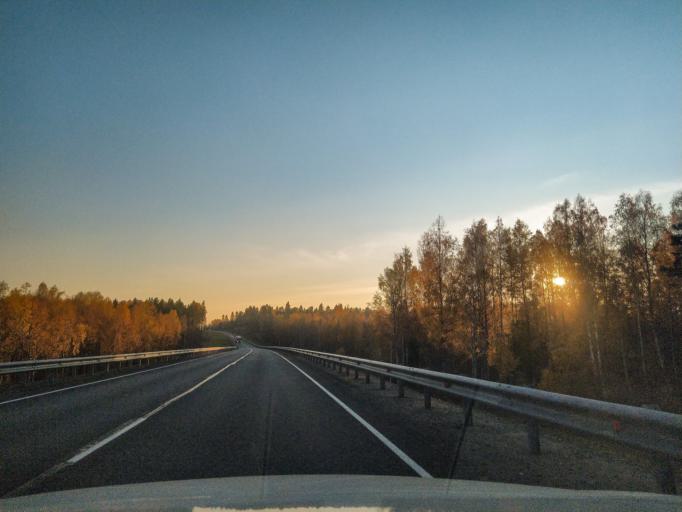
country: RU
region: Leningrad
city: Kuznechnoye
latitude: 61.3653
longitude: 29.8996
